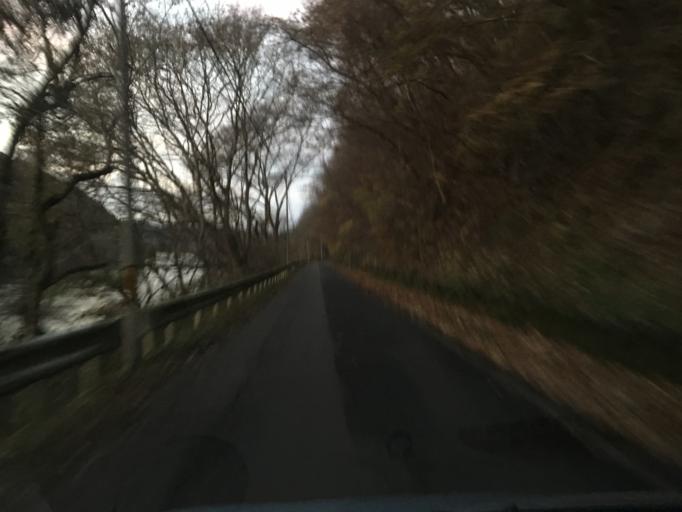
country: JP
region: Iwate
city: Ichinoseki
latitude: 38.8138
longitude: 141.2528
